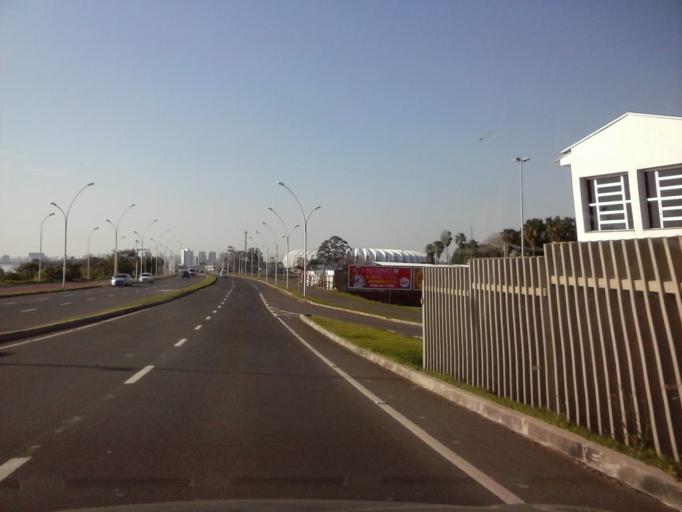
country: BR
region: Rio Grande do Sul
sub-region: Porto Alegre
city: Porto Alegre
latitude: -30.0728
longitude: -51.2412
